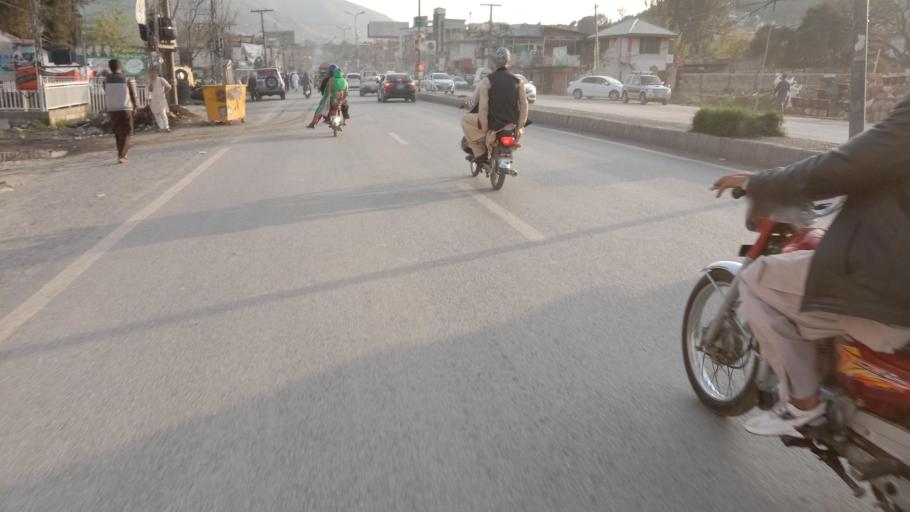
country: PK
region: Khyber Pakhtunkhwa
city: Abbottabad
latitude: 34.1721
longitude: 73.2263
